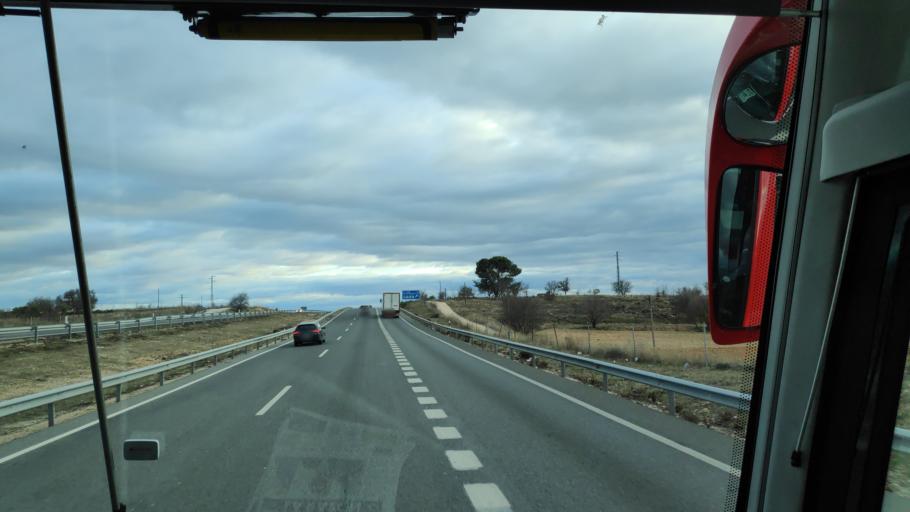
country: ES
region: Madrid
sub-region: Provincia de Madrid
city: Villarejo de Salvanes
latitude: 40.1840
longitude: -3.2976
